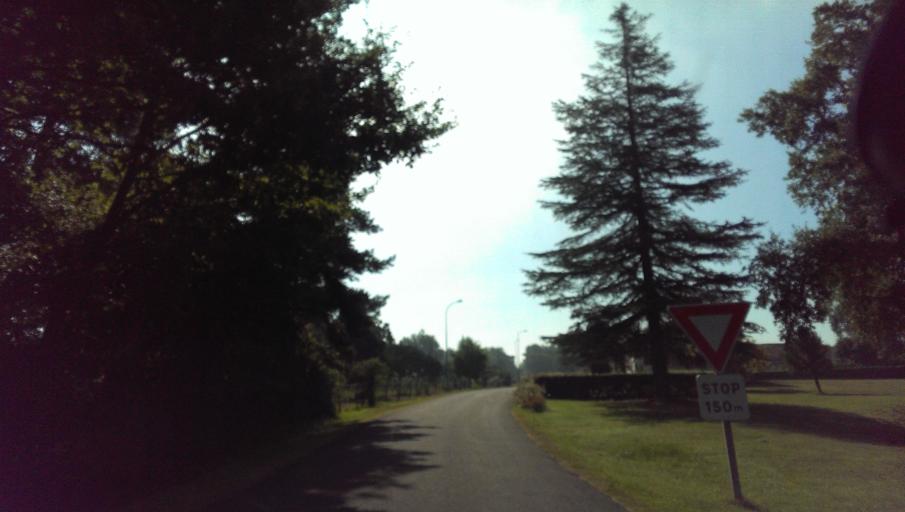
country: FR
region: Aquitaine
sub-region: Departement des Landes
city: Gabarret
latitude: 44.1036
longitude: -0.0160
